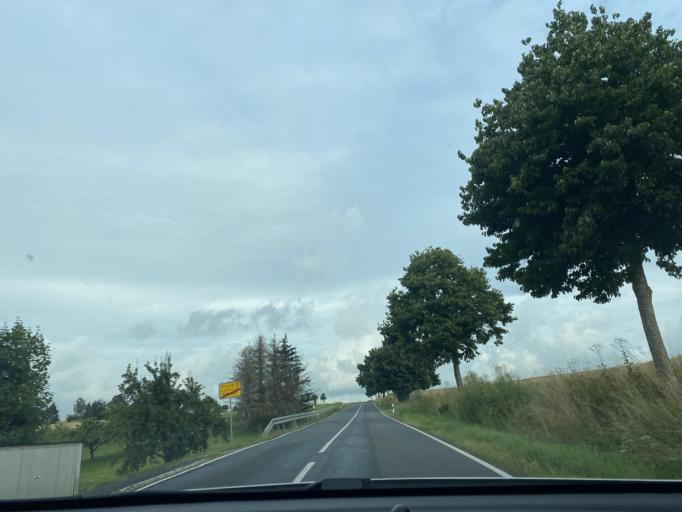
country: DE
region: Saxony
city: Grosshennersdorf
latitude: 51.0200
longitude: 14.7919
